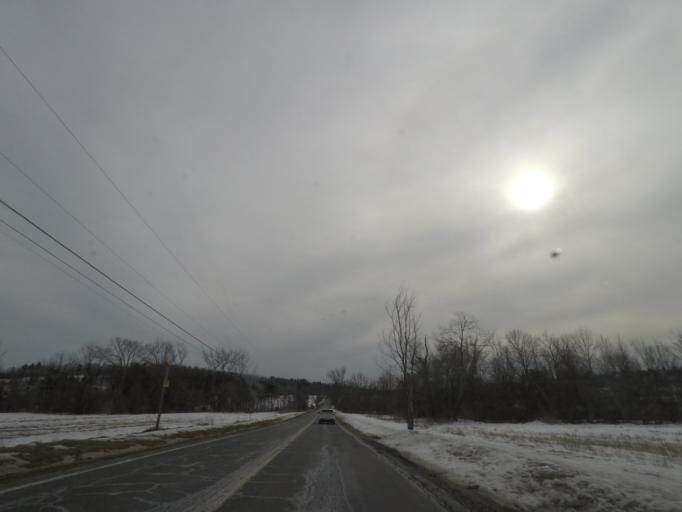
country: US
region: New York
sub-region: Albany County
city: Altamont
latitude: 42.6627
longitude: -74.1325
